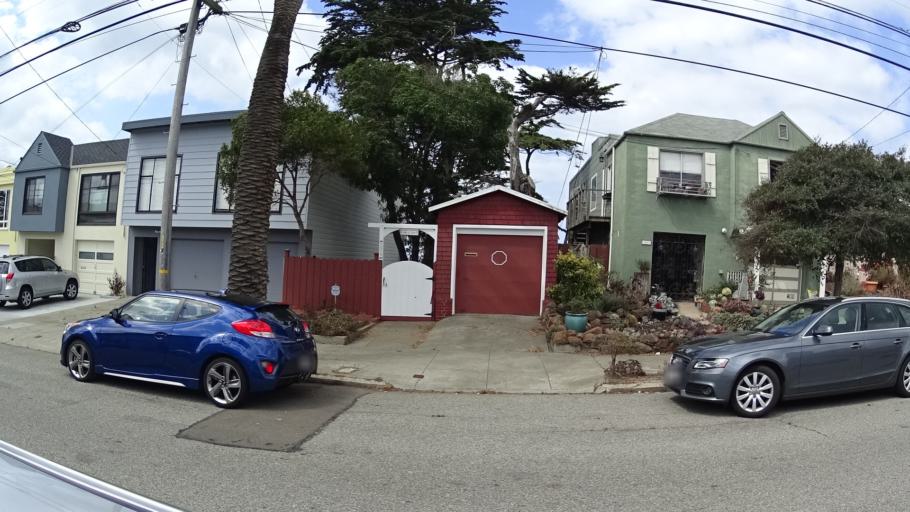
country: US
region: California
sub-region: San Mateo County
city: Daly City
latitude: 37.7571
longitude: -122.5045
